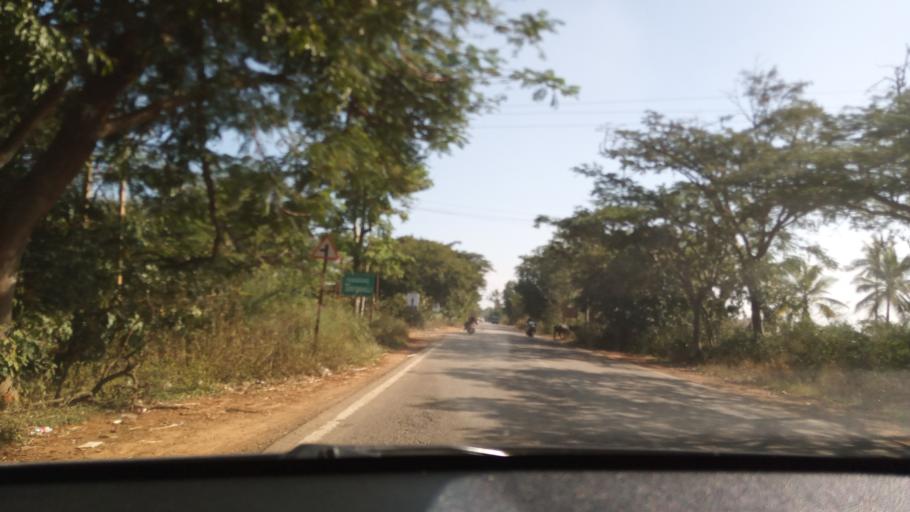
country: IN
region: Karnataka
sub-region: Bangalore Rural
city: Vijayapura
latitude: 13.2805
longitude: 77.7633
